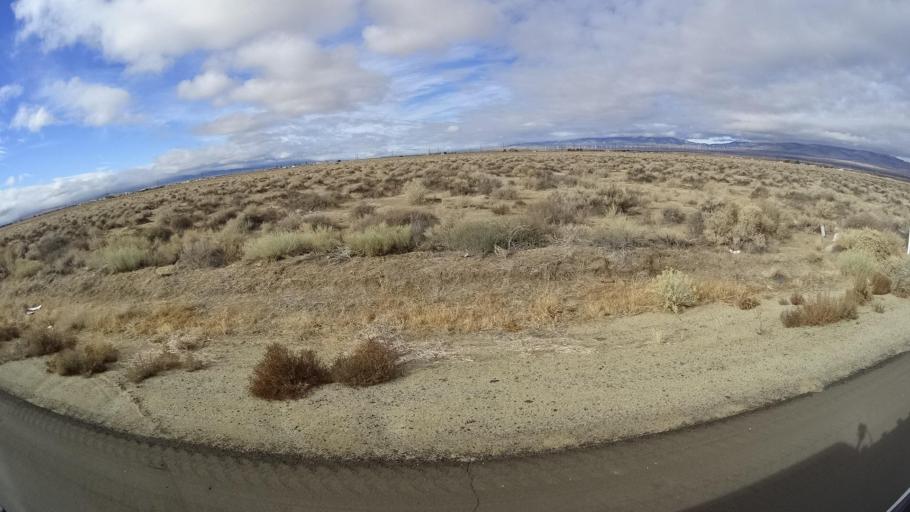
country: US
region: California
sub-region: Kern County
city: Rosamond
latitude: 34.8499
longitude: -118.2909
